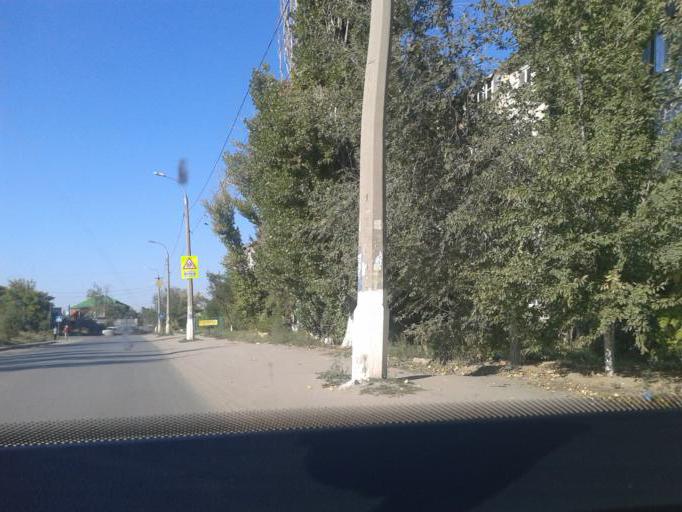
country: RU
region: Volgograd
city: Gorodishche
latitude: 48.7700
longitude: 44.4973
